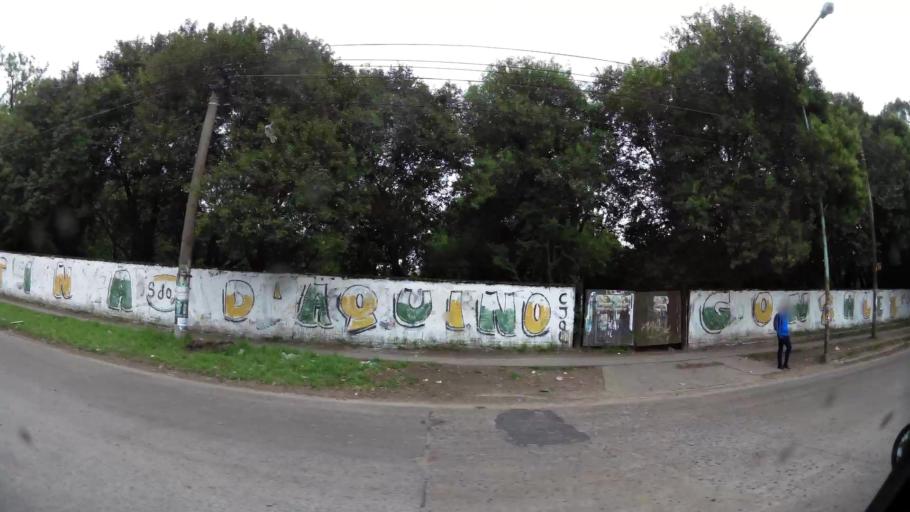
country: AR
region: Buenos Aires
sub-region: Partido de Quilmes
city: Quilmes
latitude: -34.7928
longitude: -58.2675
